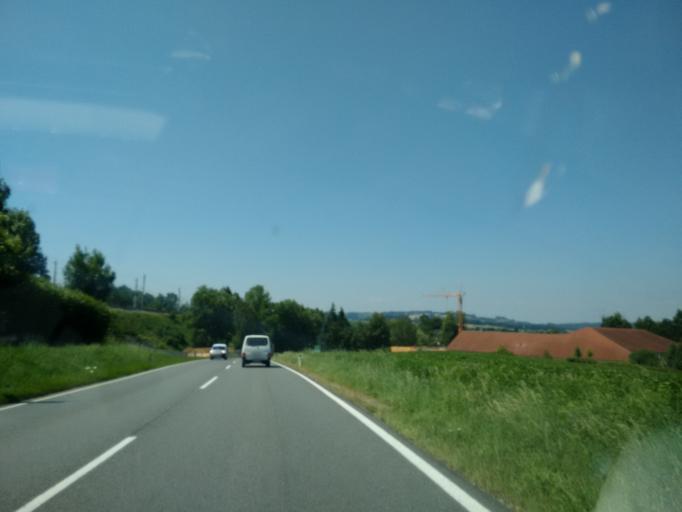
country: AT
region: Upper Austria
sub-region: Wels-Land
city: Buchkirchen
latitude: 48.2119
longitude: 13.9744
